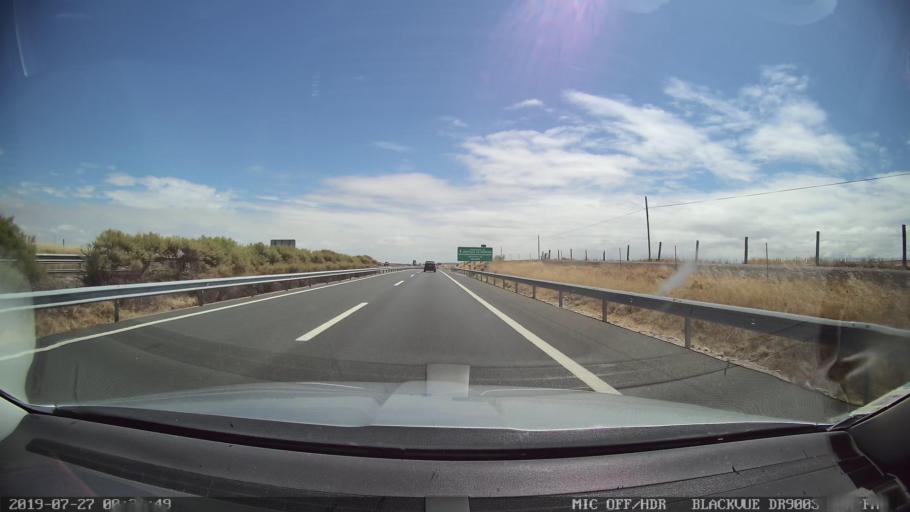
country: ES
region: Extremadura
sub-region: Provincia de Caceres
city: Peraleda de la Mata
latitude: 39.8916
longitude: -5.4011
